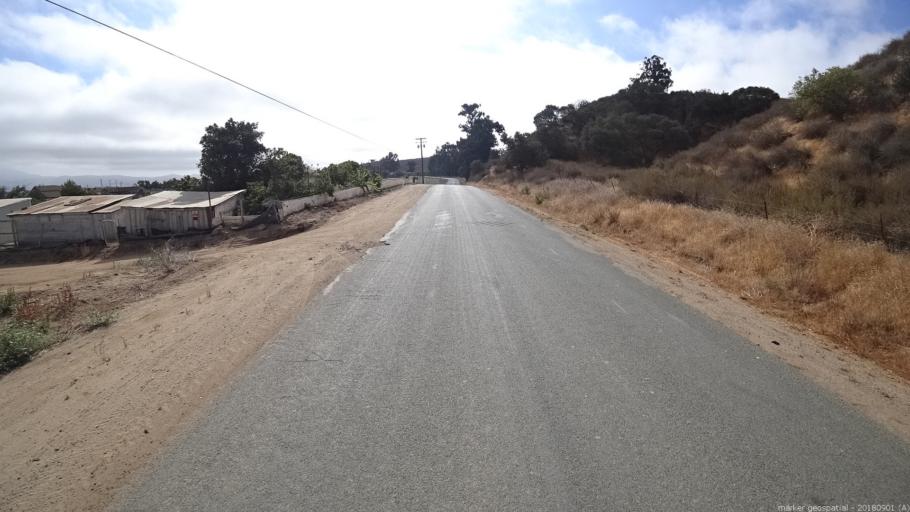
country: US
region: California
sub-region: Monterey County
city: Soledad
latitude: 36.3831
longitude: -121.3553
